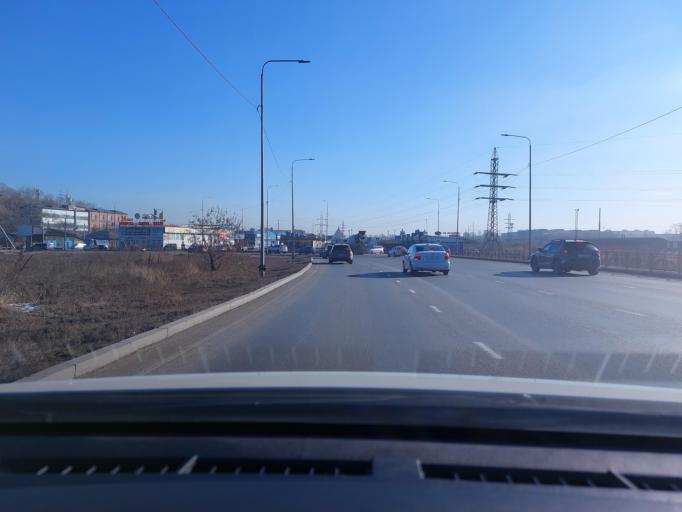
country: RU
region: Irkutsk
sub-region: Irkutskiy Rayon
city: Irkutsk
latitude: 52.2970
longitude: 104.2987
